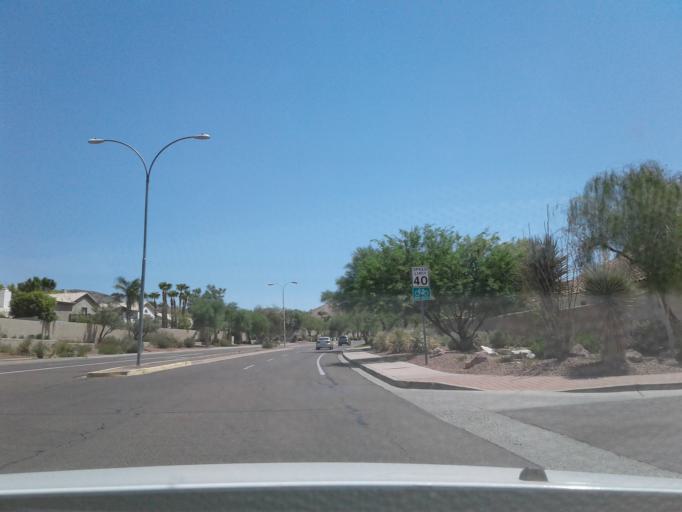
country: US
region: Arizona
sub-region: Maricopa County
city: Guadalupe
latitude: 33.3107
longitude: -112.0266
